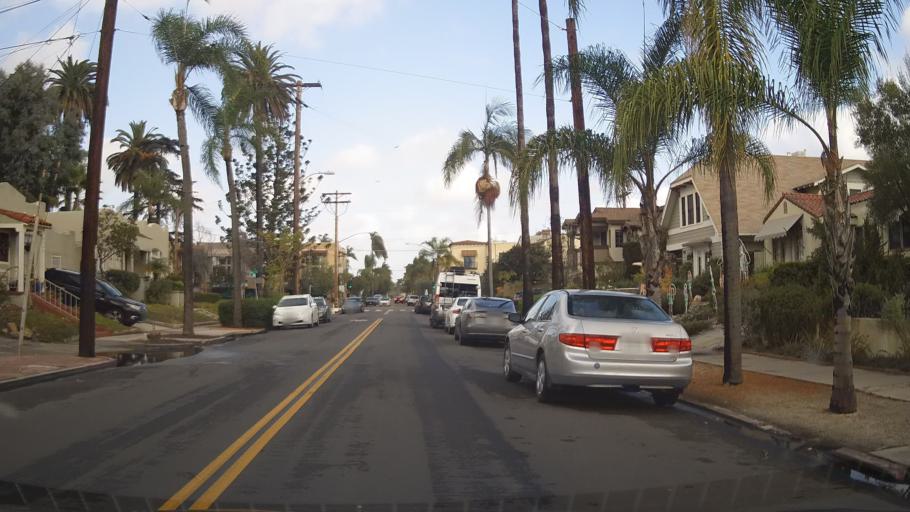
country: US
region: California
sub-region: San Diego County
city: San Diego
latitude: 32.7622
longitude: -117.1063
